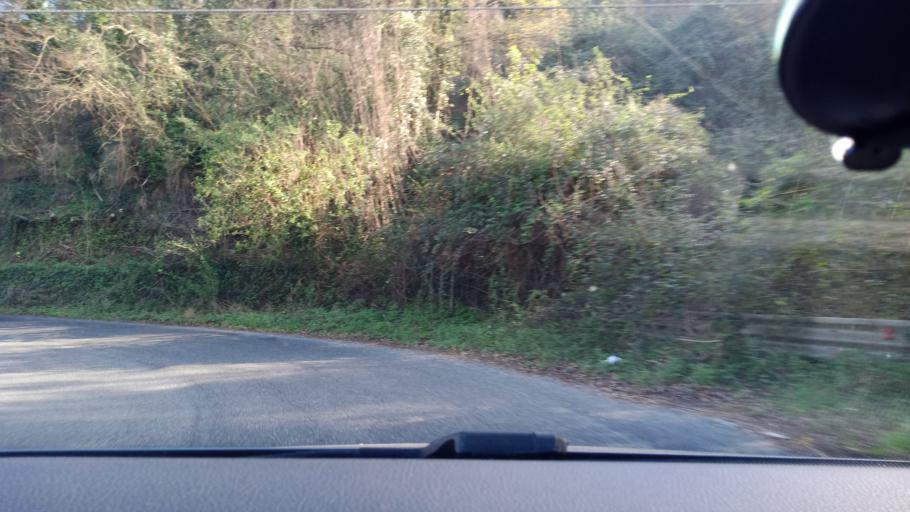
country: IT
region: Latium
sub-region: Citta metropolitana di Roma Capitale
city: Torrita Tiberina
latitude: 42.2421
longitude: 12.6205
